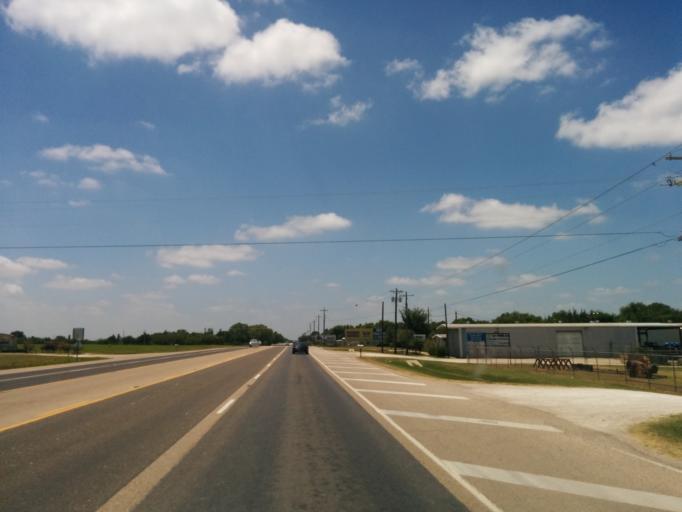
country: US
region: Texas
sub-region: Brazos County
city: Bryan
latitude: 30.7205
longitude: -96.3377
